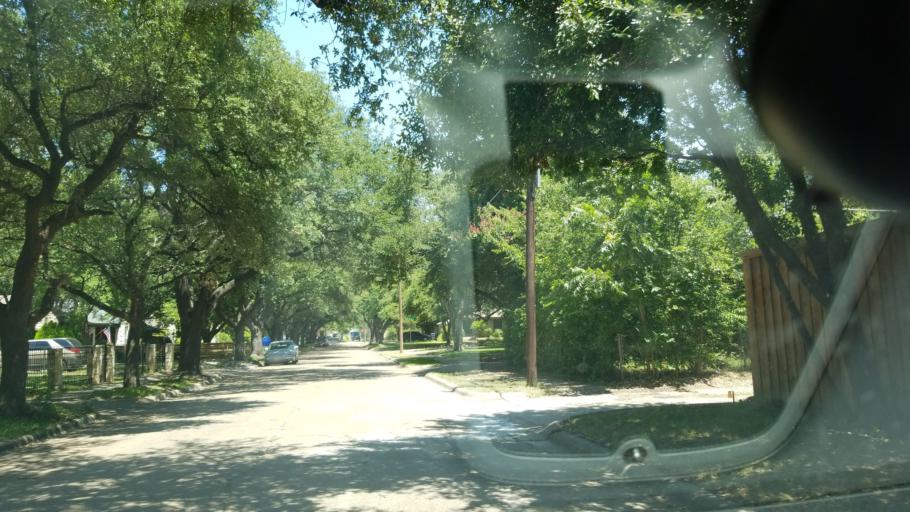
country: US
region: Texas
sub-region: Dallas County
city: Cockrell Hill
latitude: 32.7195
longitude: -96.8425
